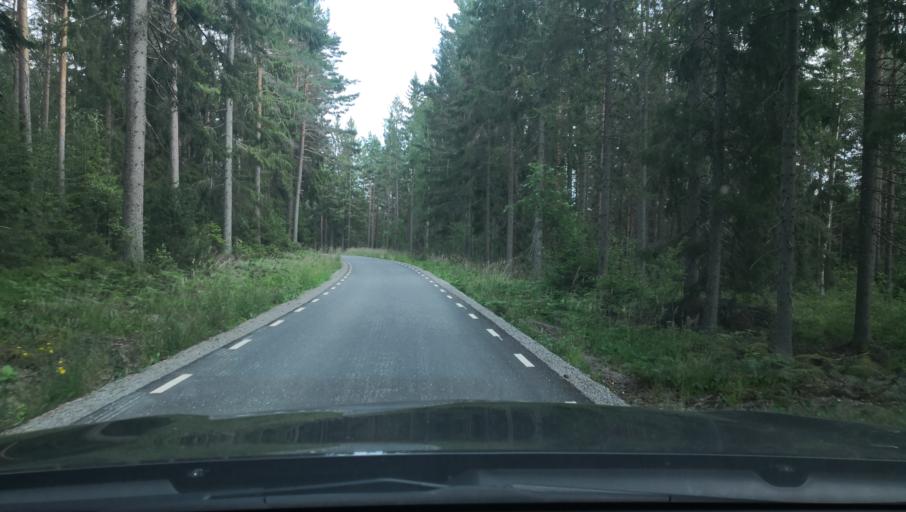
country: SE
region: Vaestmanland
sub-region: Surahammars Kommun
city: Surahammar
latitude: 59.6738
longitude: 16.1203
